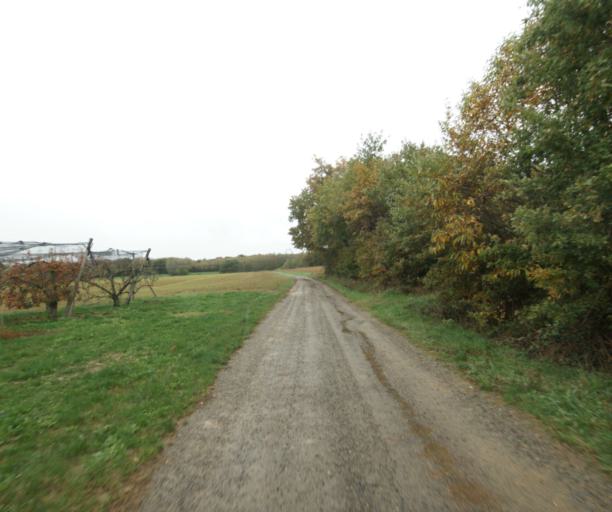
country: FR
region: Rhone-Alpes
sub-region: Departement de l'Ain
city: Pont-de-Vaux
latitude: 46.4820
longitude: 4.8568
